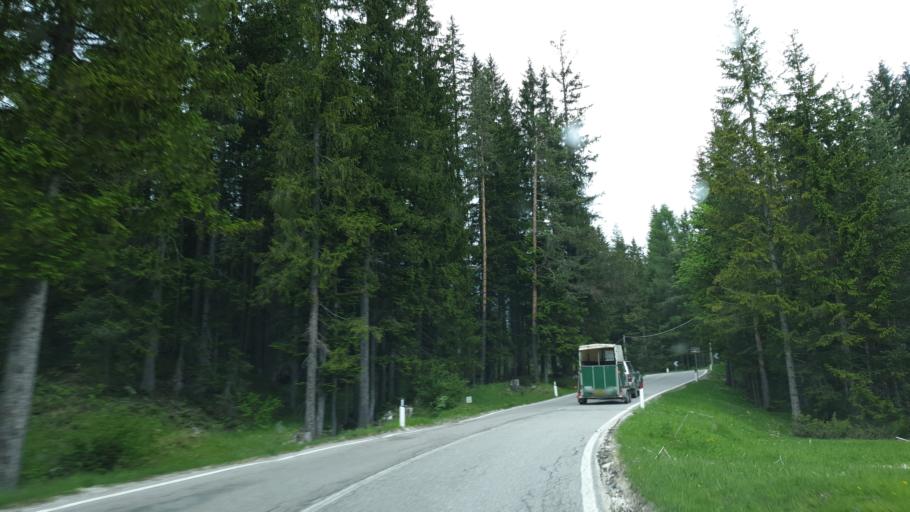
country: IT
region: Veneto
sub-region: Provincia di Belluno
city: San Vito
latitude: 46.5416
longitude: 12.2534
